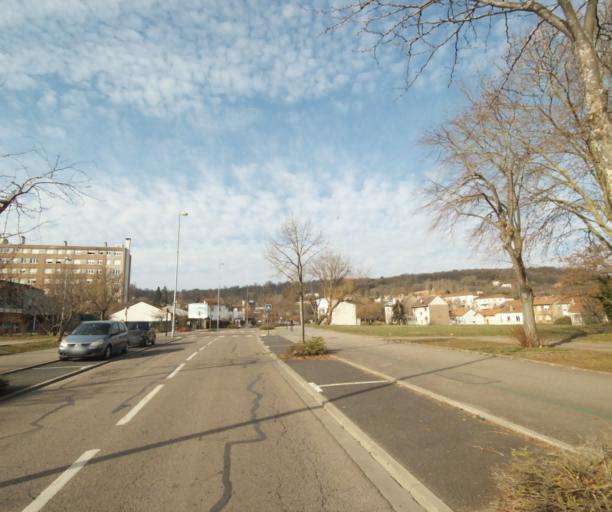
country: FR
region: Lorraine
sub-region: Departement de Meurthe-et-Moselle
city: Laxou
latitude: 48.6795
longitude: 6.1457
